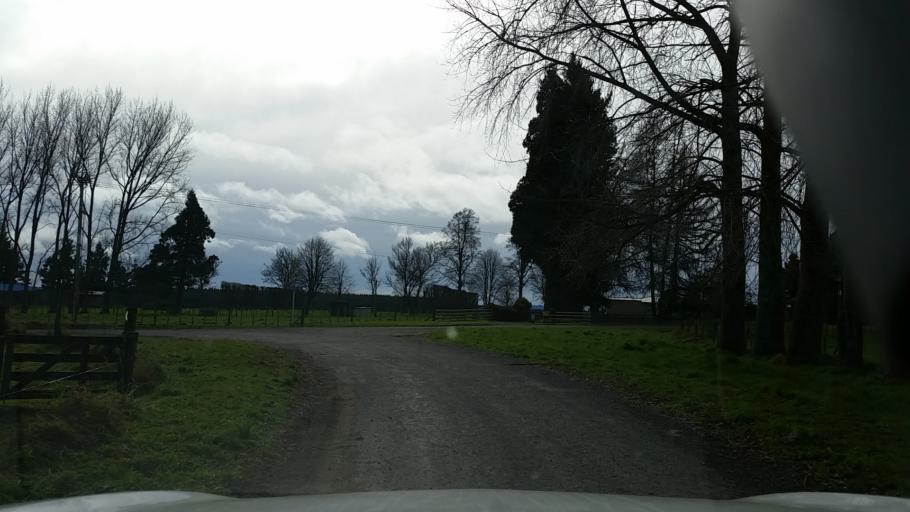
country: NZ
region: Bay of Plenty
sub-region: Whakatane District
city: Murupara
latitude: -38.4687
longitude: 176.4176
